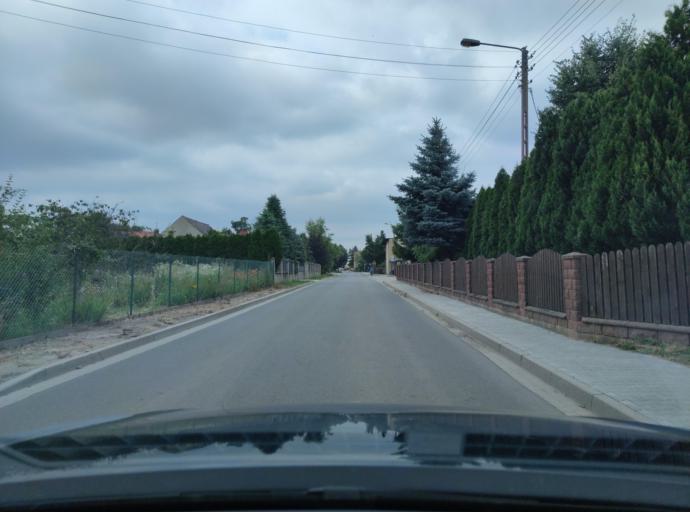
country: PL
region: Lower Silesian Voivodeship
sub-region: Powiat wroclawski
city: Tyniec Maly
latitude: 51.0026
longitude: 16.9071
